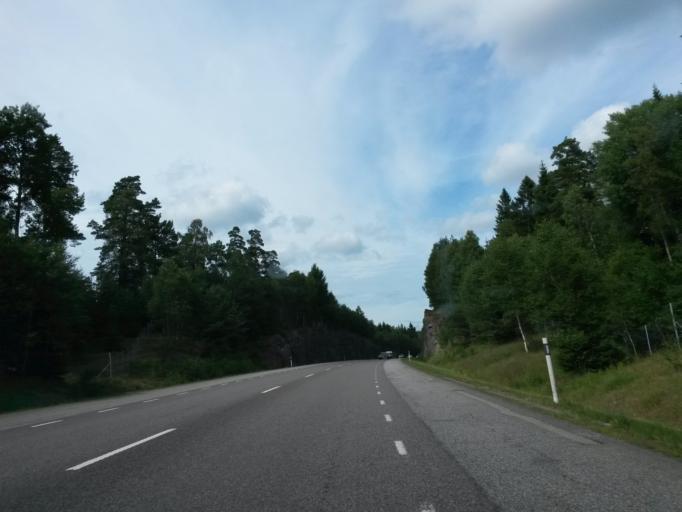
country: SE
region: Vaestra Goetaland
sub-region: Boras Kommun
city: Viskafors
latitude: 57.5917
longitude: 12.8656
